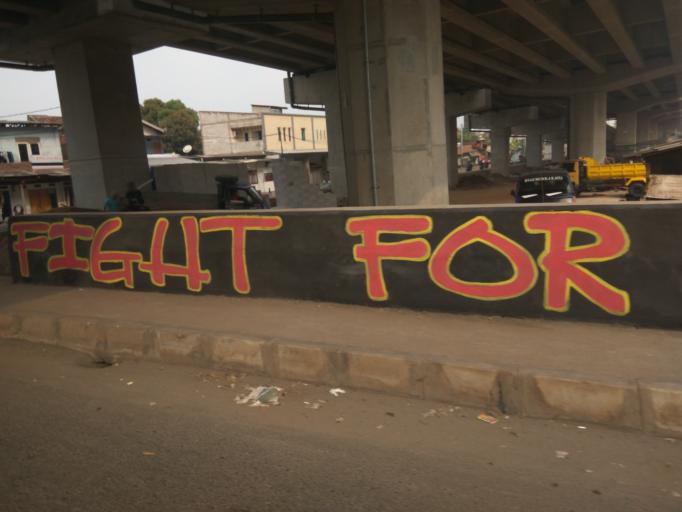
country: ID
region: West Java
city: Bekasi
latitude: -6.2498
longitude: 106.9406
